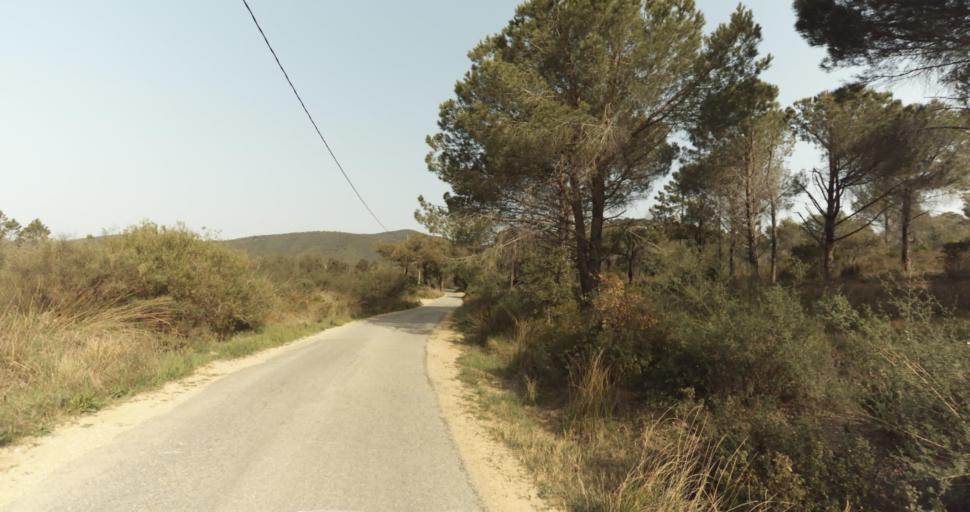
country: FR
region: Provence-Alpes-Cote d'Azur
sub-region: Departement du Var
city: Bormes-les-Mimosas
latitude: 43.1460
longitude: 6.3038
